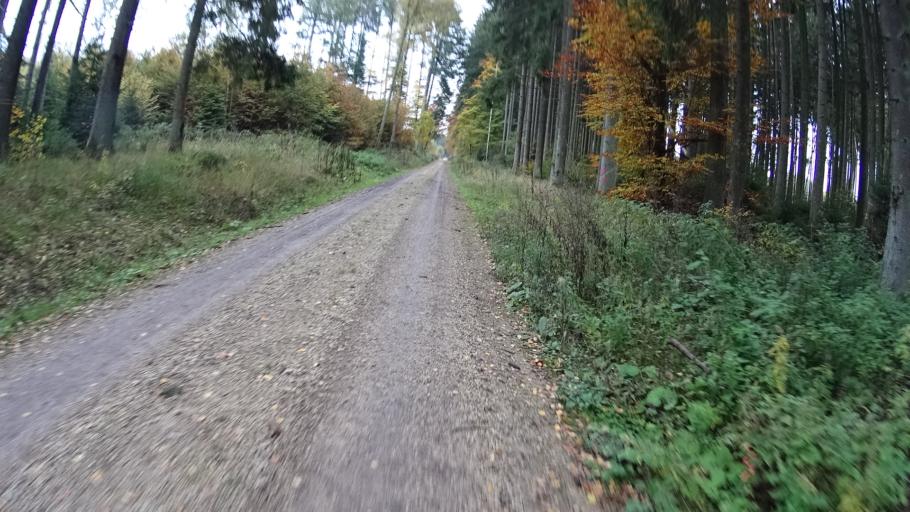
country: DE
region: Bavaria
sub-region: Upper Bavaria
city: Hitzhofen
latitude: 48.8638
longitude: 11.2921
